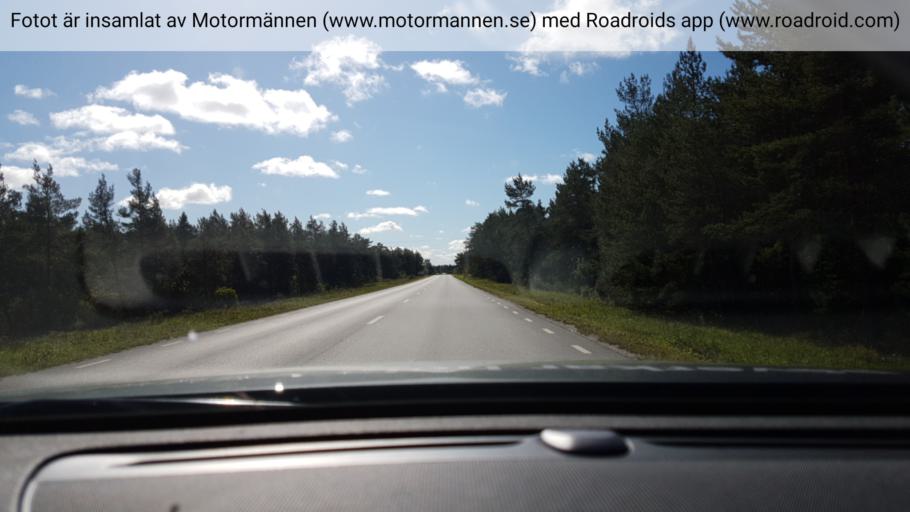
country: SE
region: Gotland
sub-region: Gotland
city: Slite
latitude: 57.7300
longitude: 18.7900
